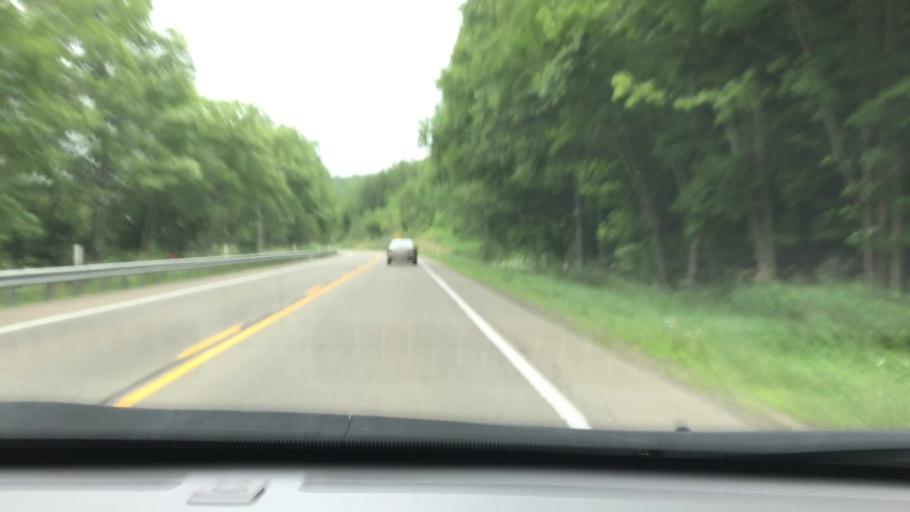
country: US
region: Pennsylvania
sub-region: Elk County
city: Johnsonburg
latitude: 41.5547
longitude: -78.6836
